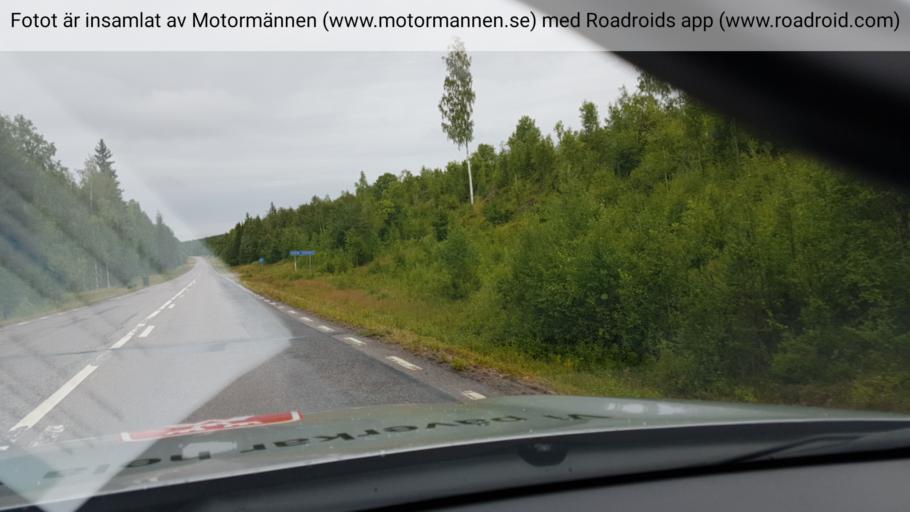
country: SE
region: Norrbotten
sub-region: Alvsbyns Kommun
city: AElvsbyn
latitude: 66.1510
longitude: 20.8751
